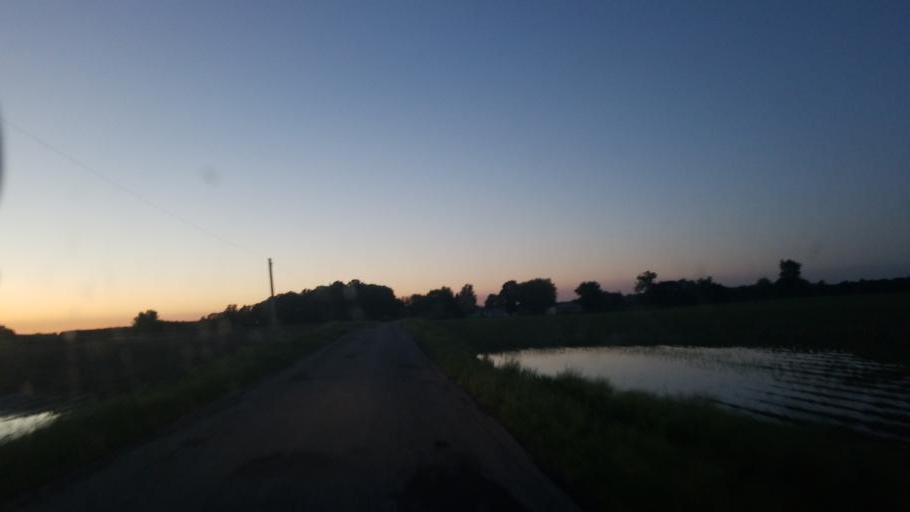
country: US
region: Indiana
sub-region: Marshall County
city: Bremen
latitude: 41.4728
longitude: -86.1177
